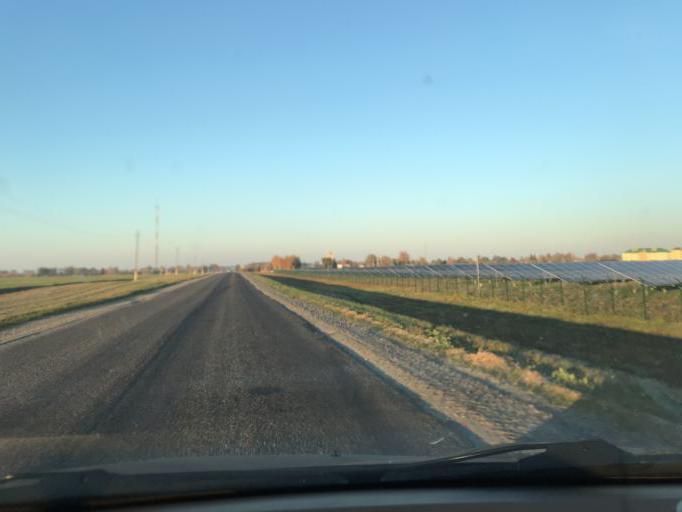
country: BY
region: Gomel
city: Brahin
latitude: 51.7824
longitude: 30.2535
